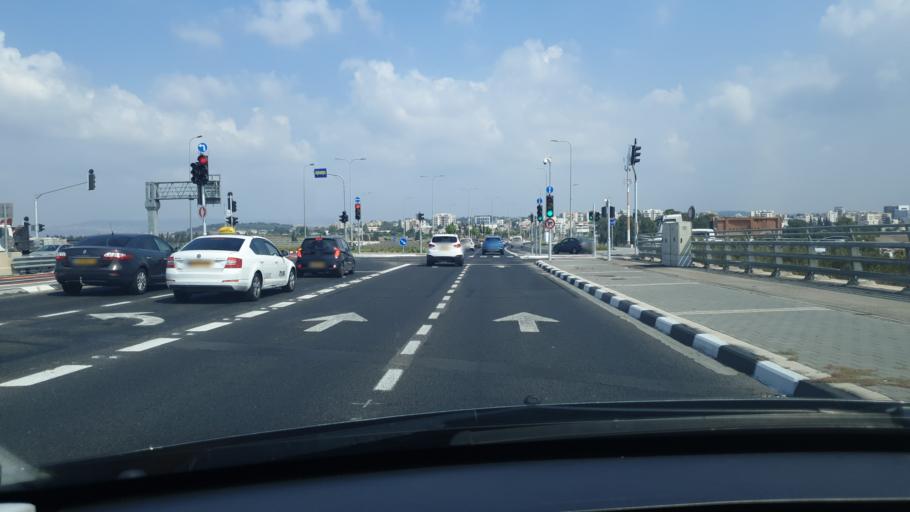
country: IL
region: Haifa
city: Qiryat Bialik
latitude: 32.8147
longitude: 35.0910
